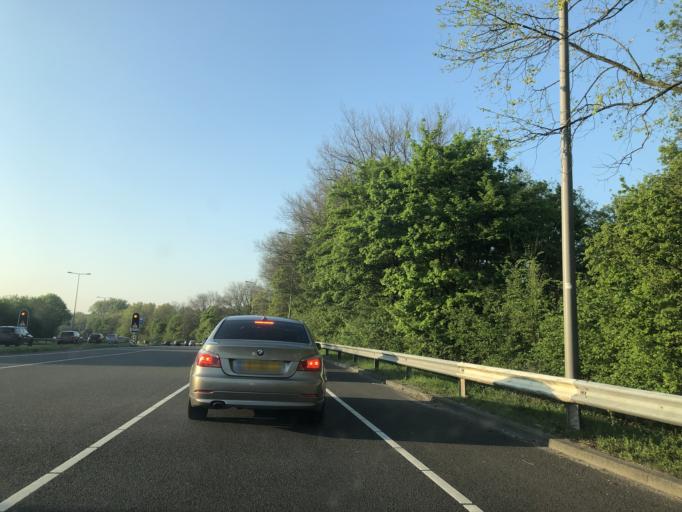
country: NL
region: South Holland
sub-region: Gemeente Barendrecht
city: Barendrecht
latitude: 51.8698
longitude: 4.5155
